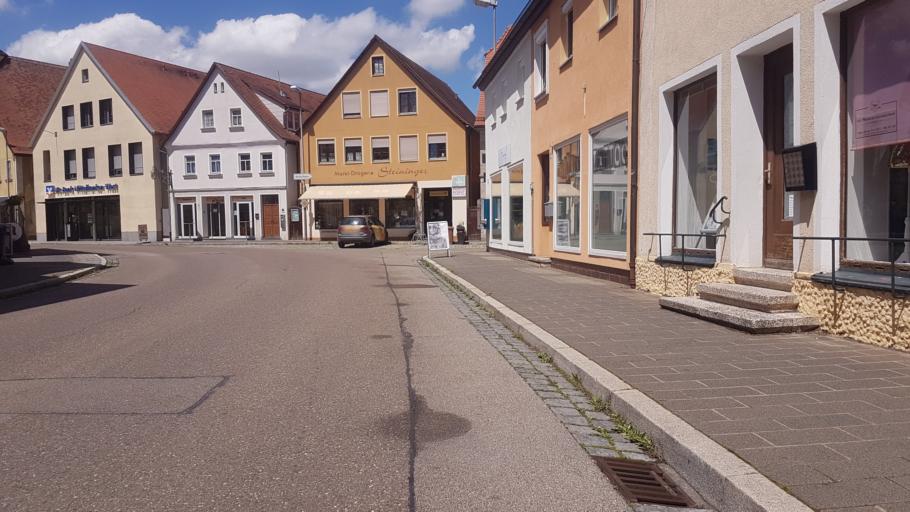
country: DE
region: Bavaria
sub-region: Regierungsbezirk Mittelfranken
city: Leutershausen
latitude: 49.2995
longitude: 10.4091
